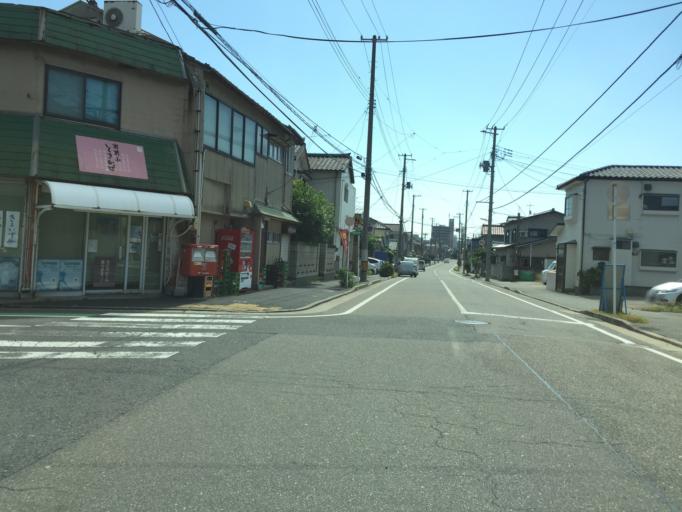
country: JP
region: Niigata
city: Niigata-shi
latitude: 37.9343
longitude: 139.0495
